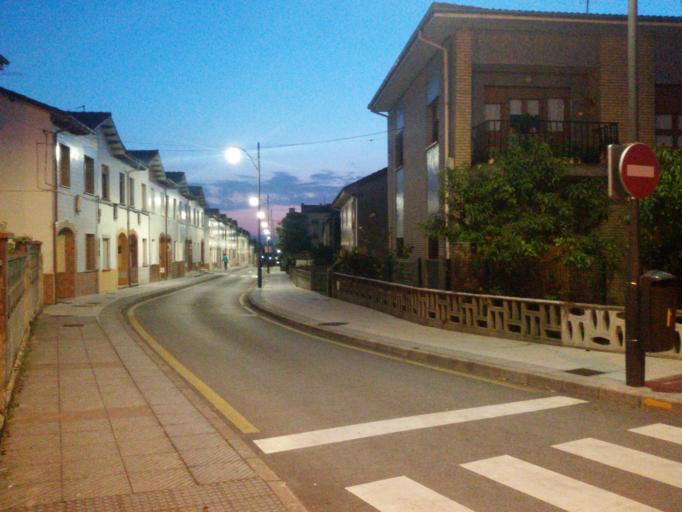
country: ES
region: Asturias
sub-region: Province of Asturias
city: Norena
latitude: 43.3837
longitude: -5.7083
